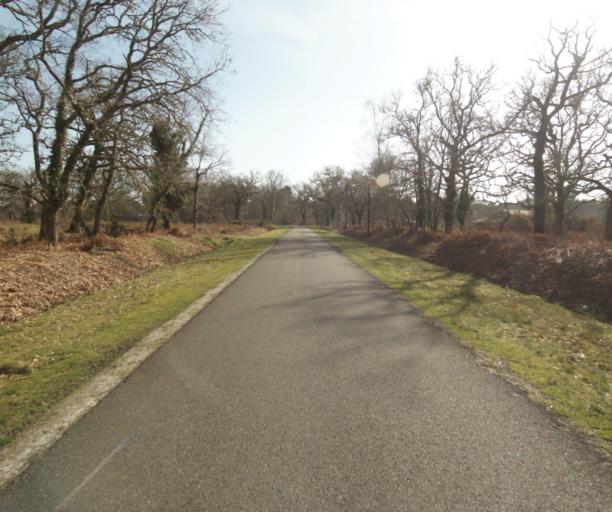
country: FR
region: Aquitaine
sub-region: Departement de la Gironde
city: Grignols
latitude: 44.2335
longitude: -0.1565
